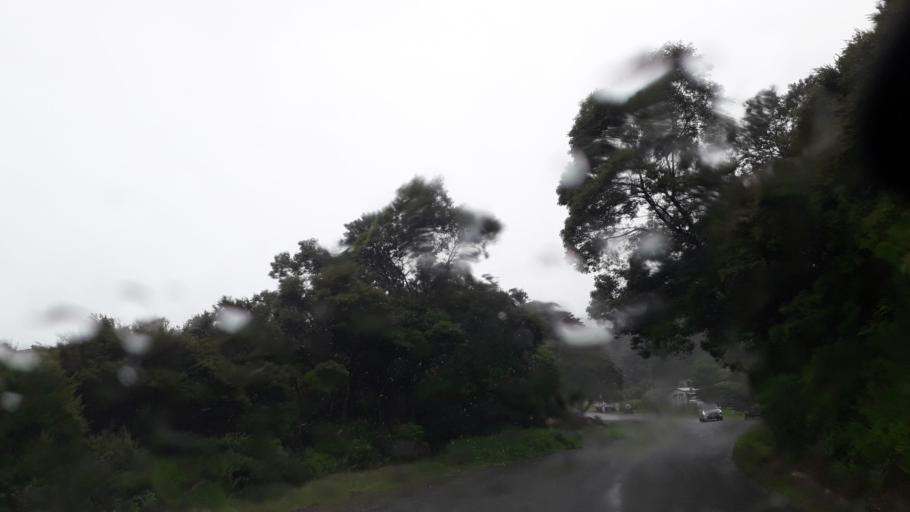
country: NZ
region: Northland
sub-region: Far North District
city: Paihia
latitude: -35.2332
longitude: 174.2606
